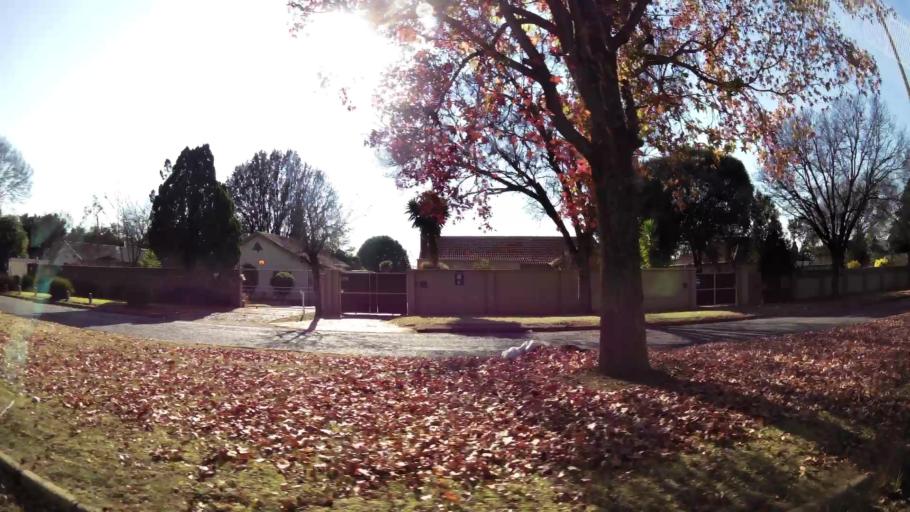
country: ZA
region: Gauteng
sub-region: City of Johannesburg Metropolitan Municipality
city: Modderfontein
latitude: -26.1505
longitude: 28.1650
